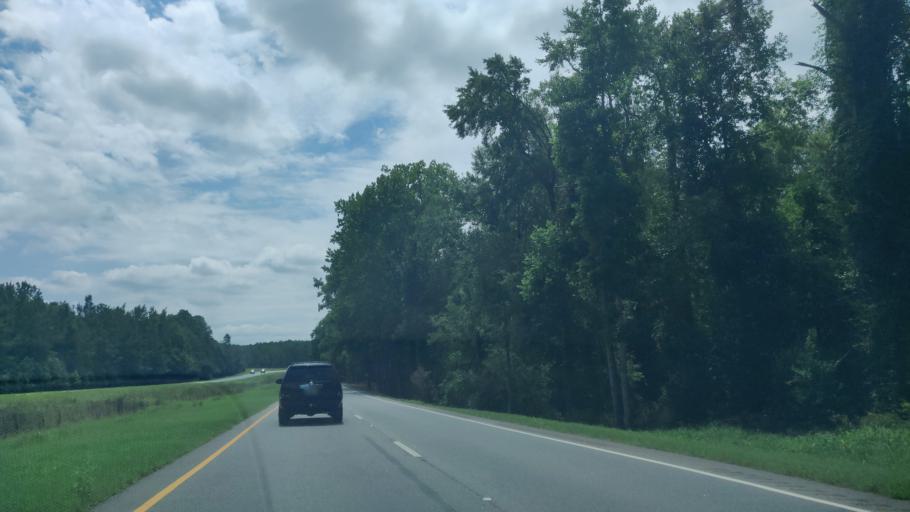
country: US
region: Georgia
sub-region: Terrell County
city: Dawson
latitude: 31.8702
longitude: -84.4902
